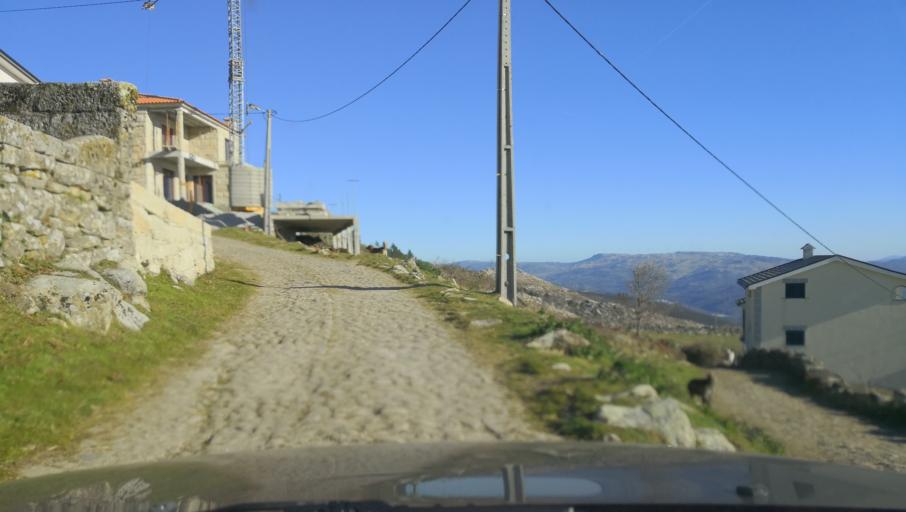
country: PT
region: Vila Real
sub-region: Vila Real
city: Vila Real
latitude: 41.3487
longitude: -7.7627
